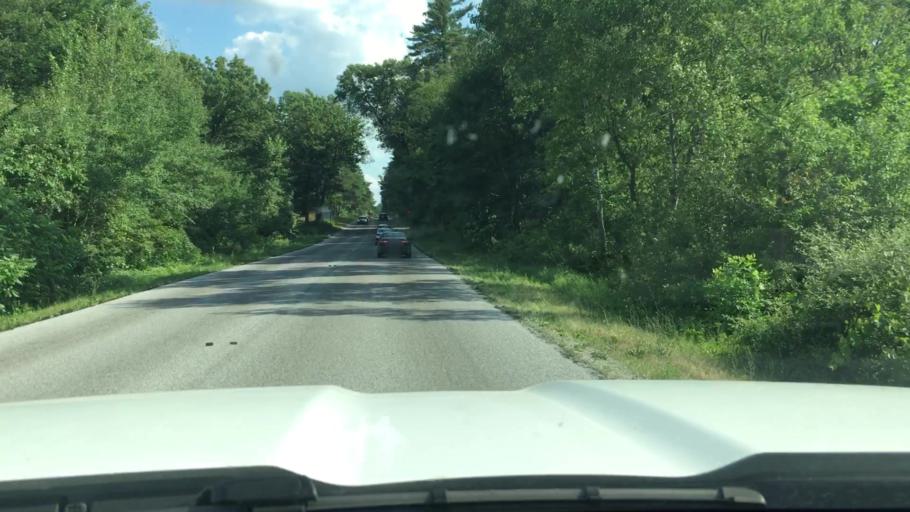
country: US
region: Michigan
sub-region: Montcalm County
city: Greenville
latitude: 43.1708
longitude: -85.3528
